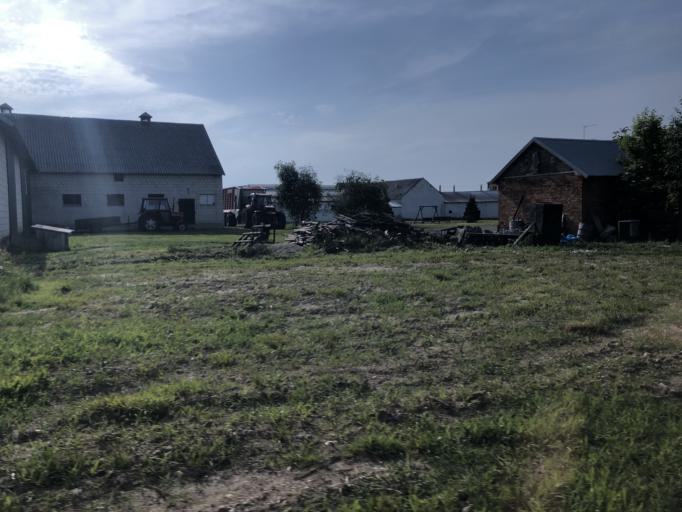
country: PL
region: Podlasie
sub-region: Lomza
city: Lomza
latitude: 53.1439
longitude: 22.0071
